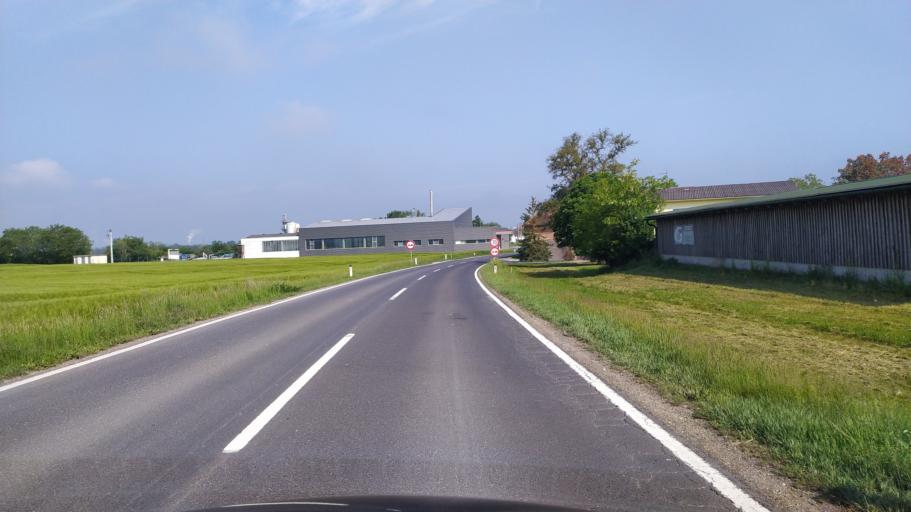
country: AT
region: Lower Austria
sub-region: Politischer Bezirk Amstetten
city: Ennsdorf
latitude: 48.2135
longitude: 14.5424
